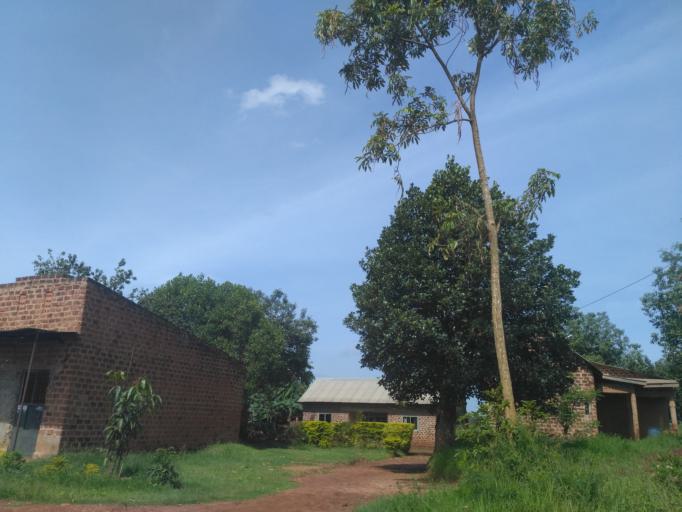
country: UG
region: Central Region
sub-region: Wakiso District
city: Kireka
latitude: 0.4514
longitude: 32.5823
